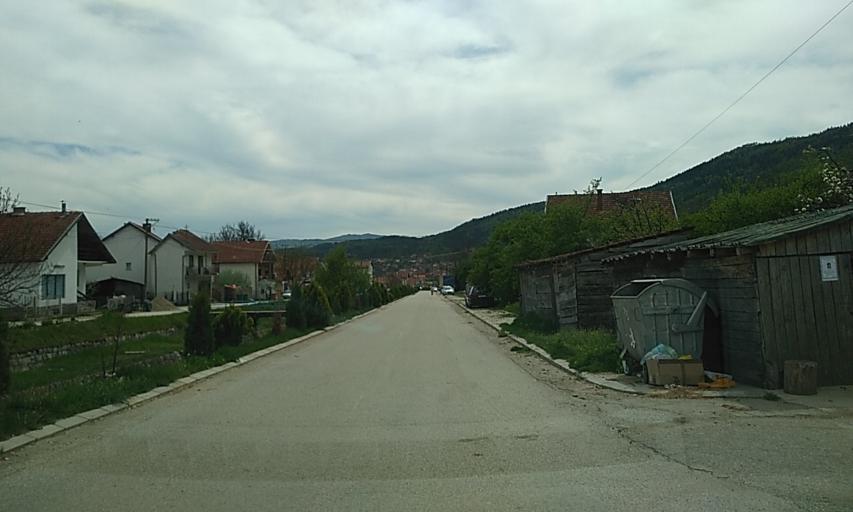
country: RS
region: Central Serbia
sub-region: Pcinjski Okrug
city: Bosilegrad
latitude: 42.5040
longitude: 22.4746
